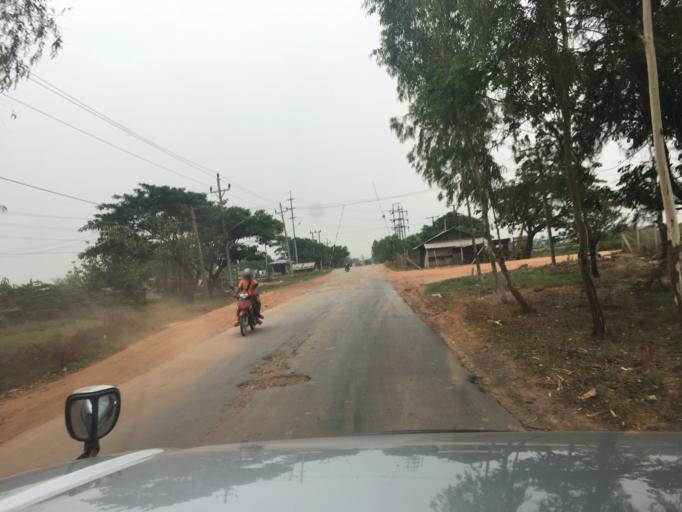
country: MM
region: Yangon
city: Syriam
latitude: 16.9494
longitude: 96.2780
